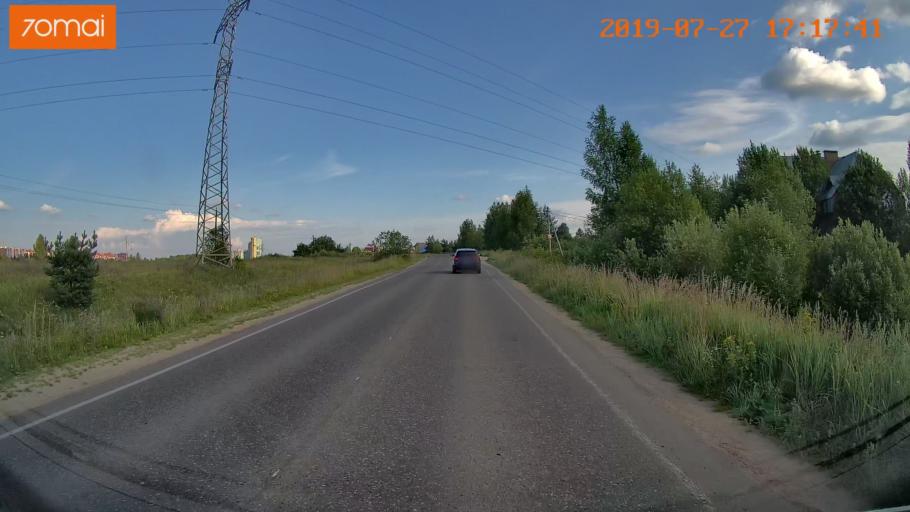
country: RU
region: Ivanovo
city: Novo-Talitsy
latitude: 57.0352
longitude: 40.8973
